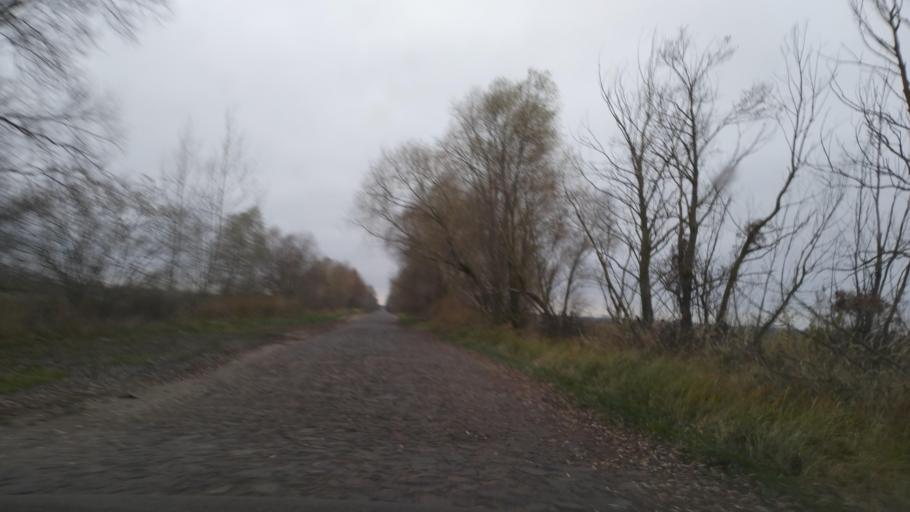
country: BY
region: Brest
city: Davyd-Haradok
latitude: 51.9939
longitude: 27.2055
